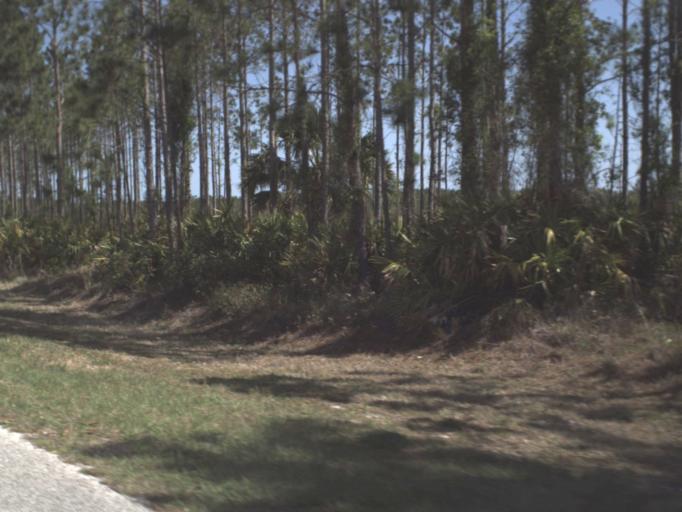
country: US
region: Florida
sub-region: Flagler County
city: Palm Coast
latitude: 29.6260
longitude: -81.2828
